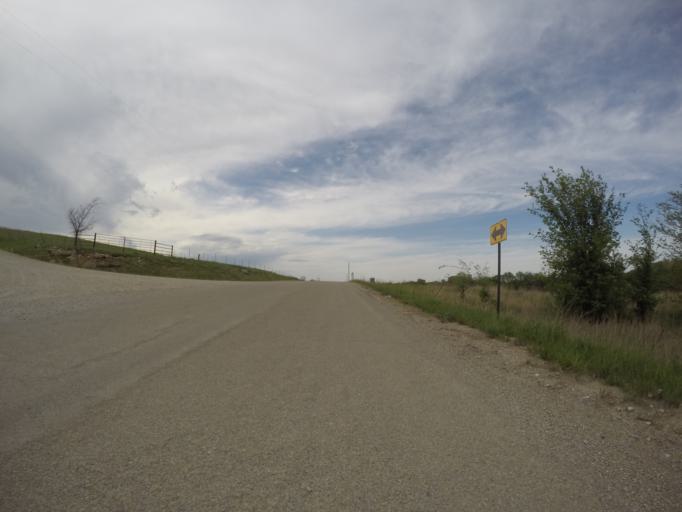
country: US
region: Kansas
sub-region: Riley County
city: Ogden
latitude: 39.0070
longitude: -96.6026
